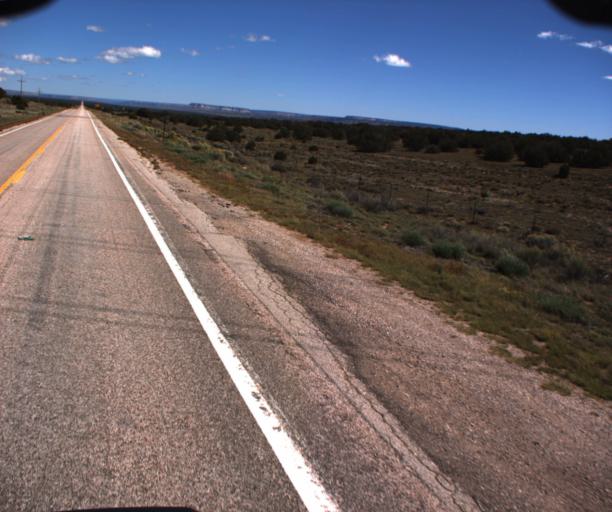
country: US
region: New Mexico
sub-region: McKinley County
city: Zuni Pueblo
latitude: 35.0200
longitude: -109.0458
